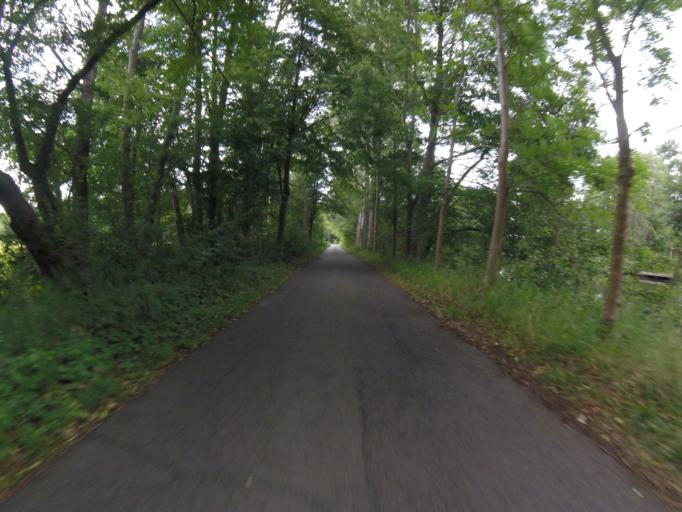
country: DE
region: Brandenburg
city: Halbe
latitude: 52.1033
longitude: 13.7666
